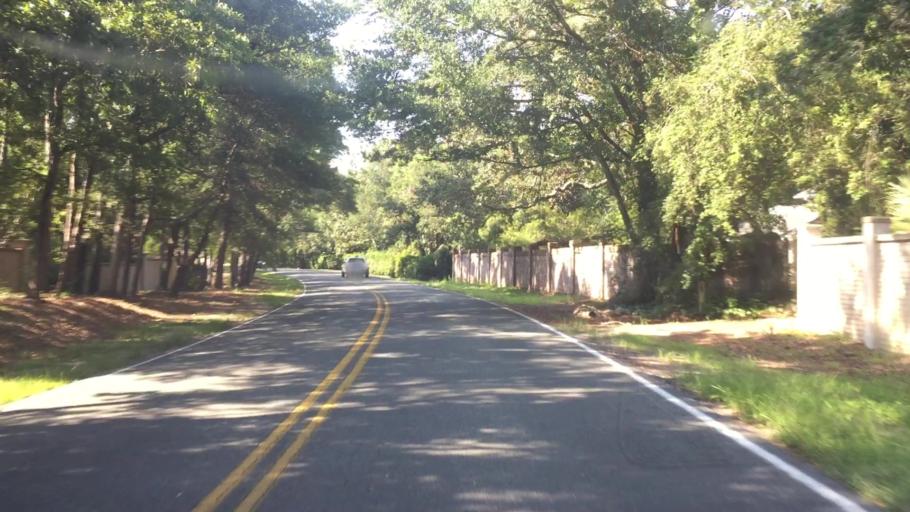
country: US
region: South Carolina
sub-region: Horry County
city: Myrtle Beach
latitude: 33.7546
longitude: -78.8058
